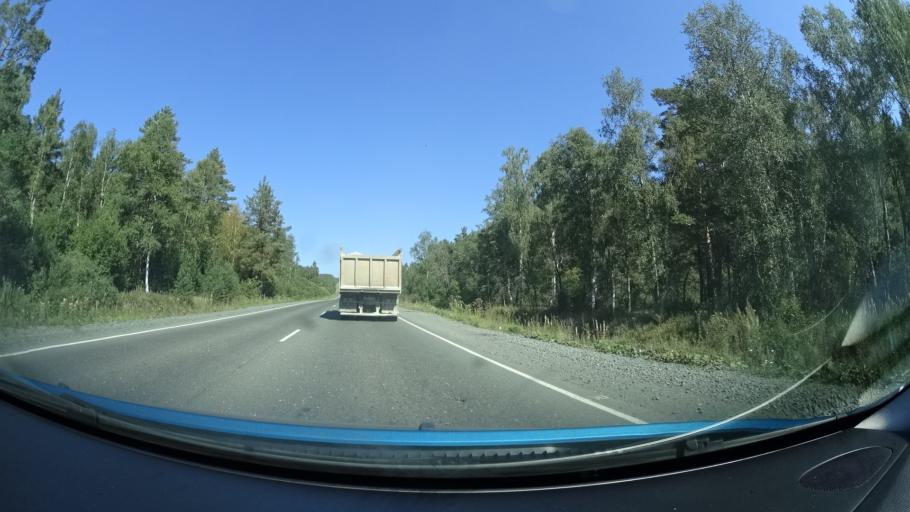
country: RU
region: Bashkortostan
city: Abzakovo
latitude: 53.8698
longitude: 58.5380
